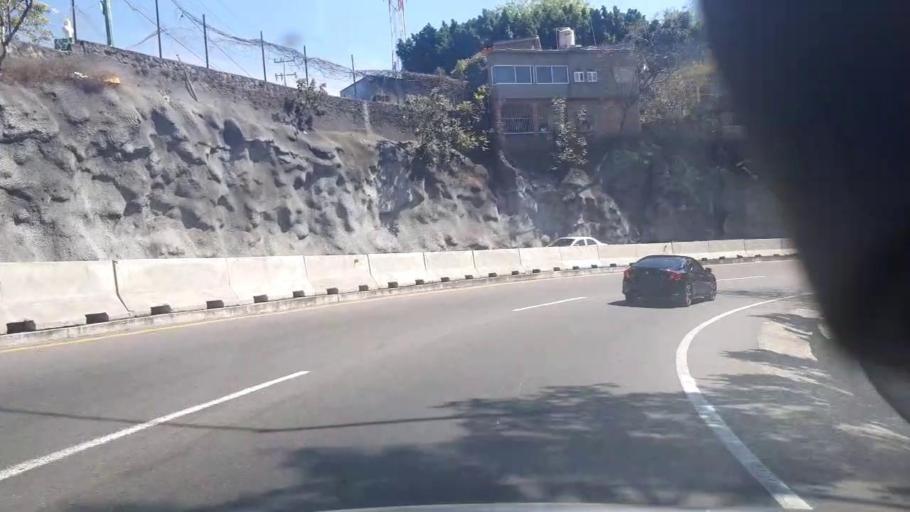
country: MX
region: Morelos
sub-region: Cuernavaca
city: Fraccionamiento Lomas de Ahuatlan
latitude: 18.9702
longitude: -99.2381
